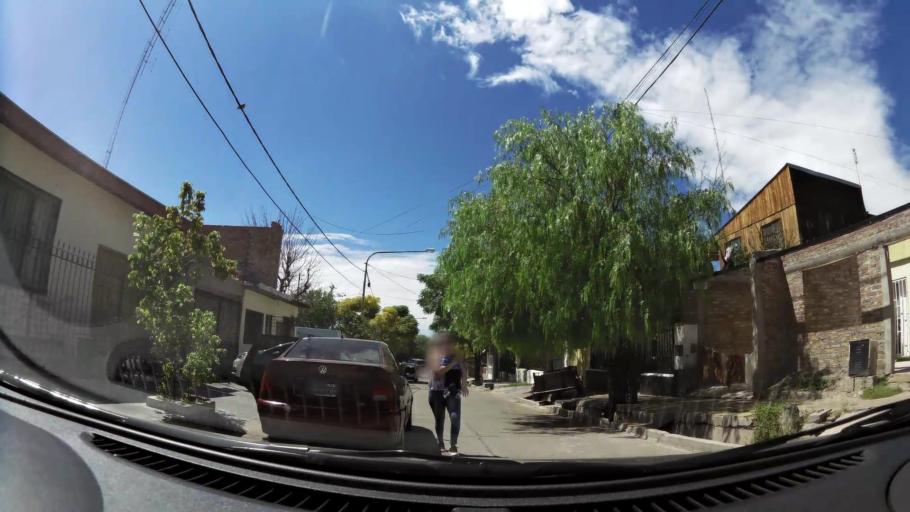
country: AR
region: Mendoza
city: Las Heras
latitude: -32.8633
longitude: -68.8673
